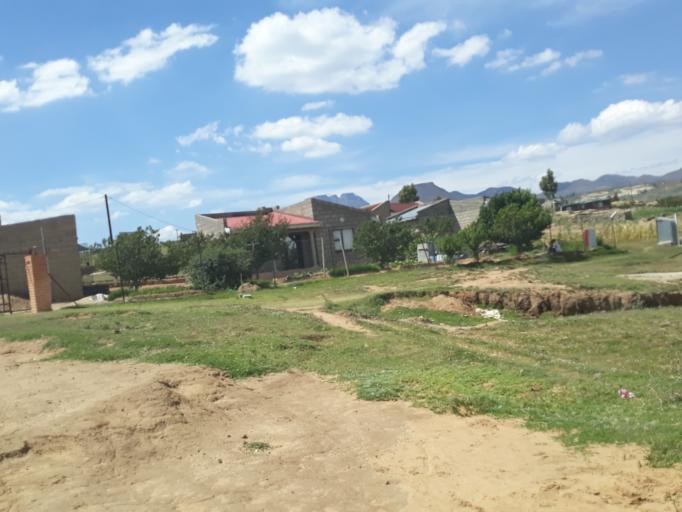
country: LS
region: Mohale's Hoek District
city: Mohale's Hoek
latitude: -30.1023
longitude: 27.4649
